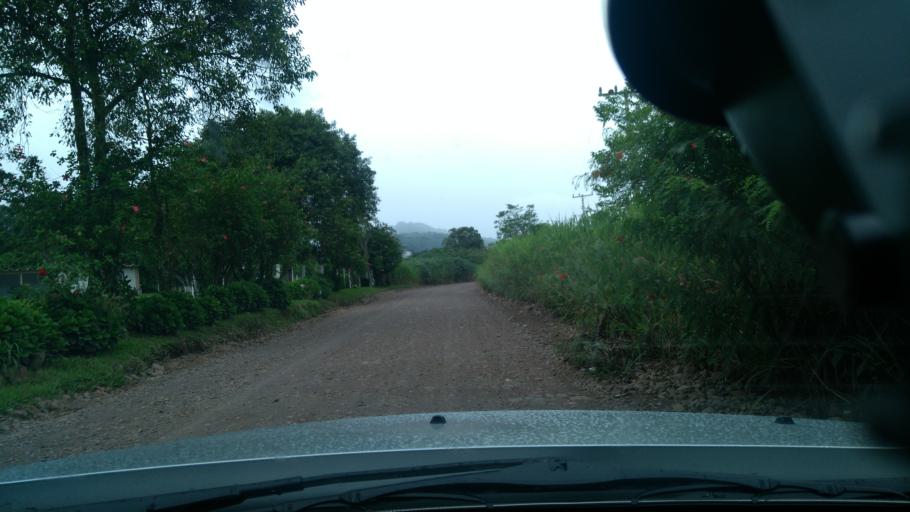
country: BR
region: Rio Grande do Sul
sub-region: Torres
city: Torres
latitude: -29.2116
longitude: -49.9817
